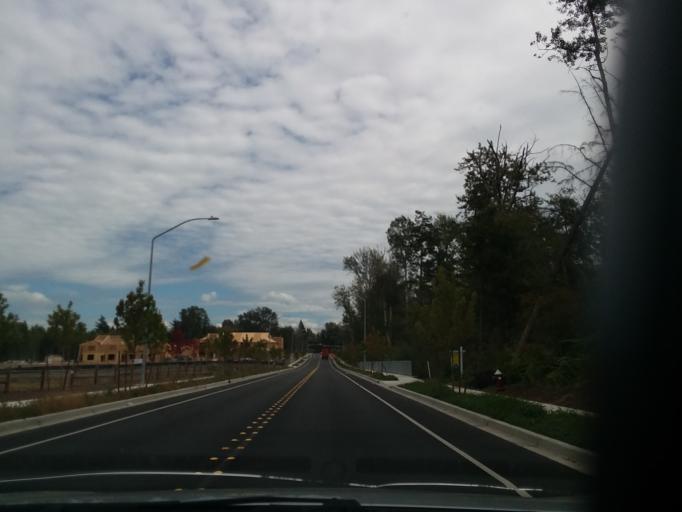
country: US
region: Washington
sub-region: Whatcom County
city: Marietta-Alderwood
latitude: 48.7932
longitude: -122.5197
